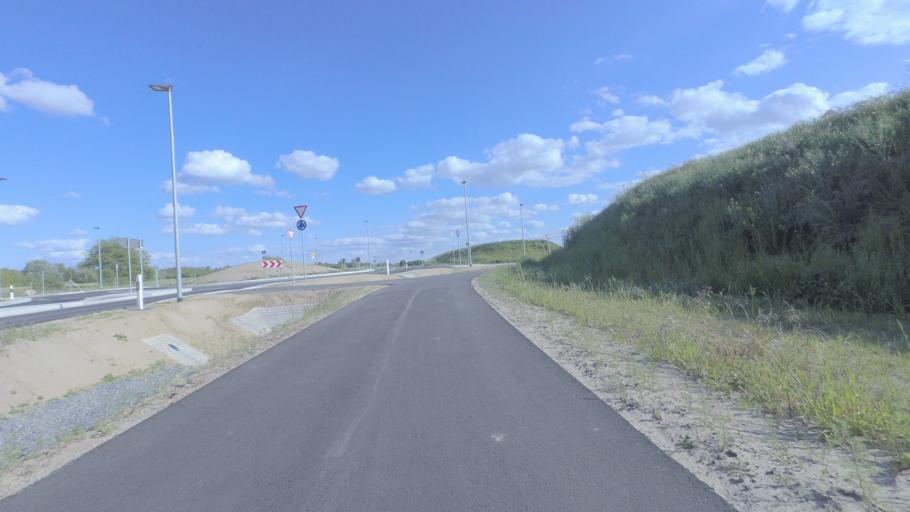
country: DE
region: Brandenburg
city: Stahnsdorf
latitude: 52.3801
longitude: 13.2341
